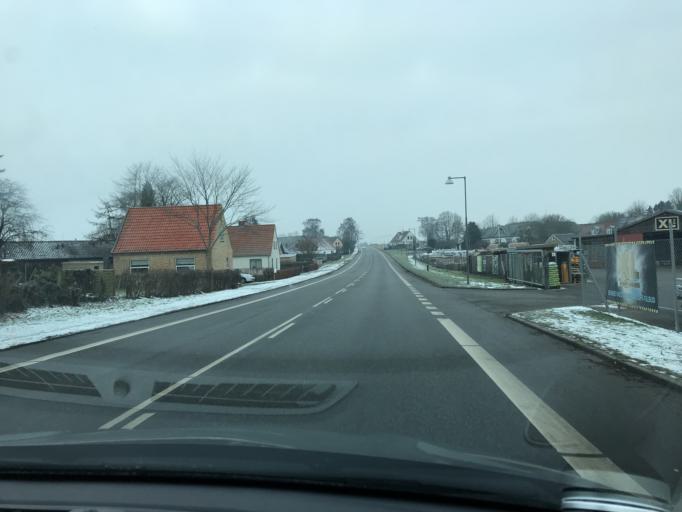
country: DK
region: Zealand
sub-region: Odsherred Kommune
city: Horve
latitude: 55.7561
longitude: 11.4535
